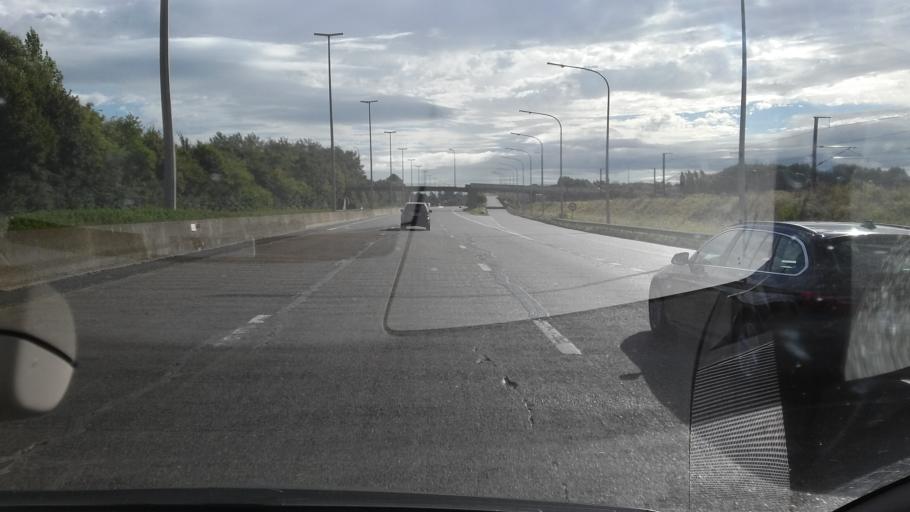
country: BE
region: Wallonia
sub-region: Province de Liege
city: Waremme
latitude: 50.7065
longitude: 5.2394
